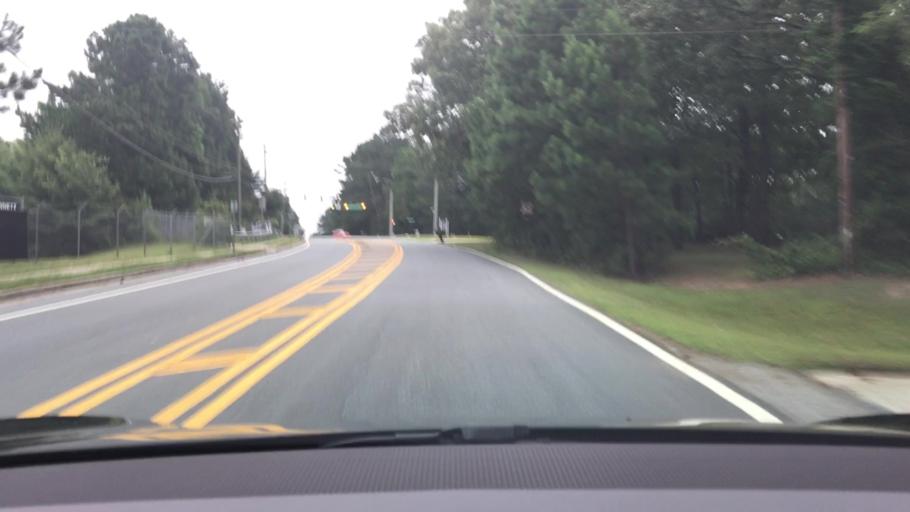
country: US
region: Georgia
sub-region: Gwinnett County
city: Suwanee
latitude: 34.0853
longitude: -84.0687
